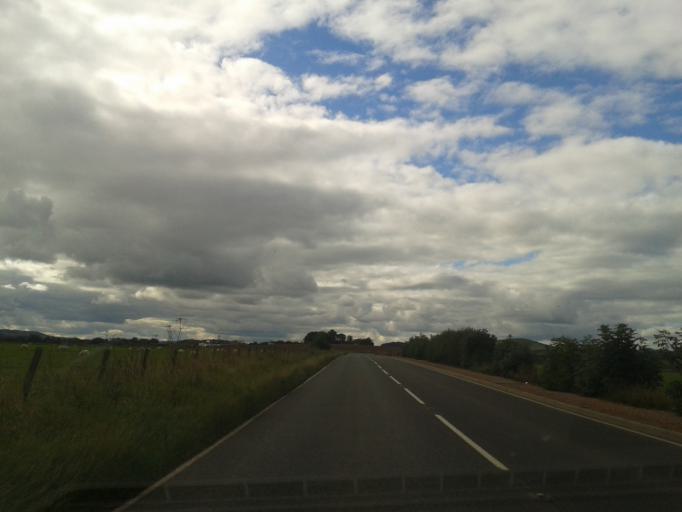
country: GB
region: Scotland
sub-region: Fife
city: Balmullo
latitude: 56.3591
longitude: -2.9041
